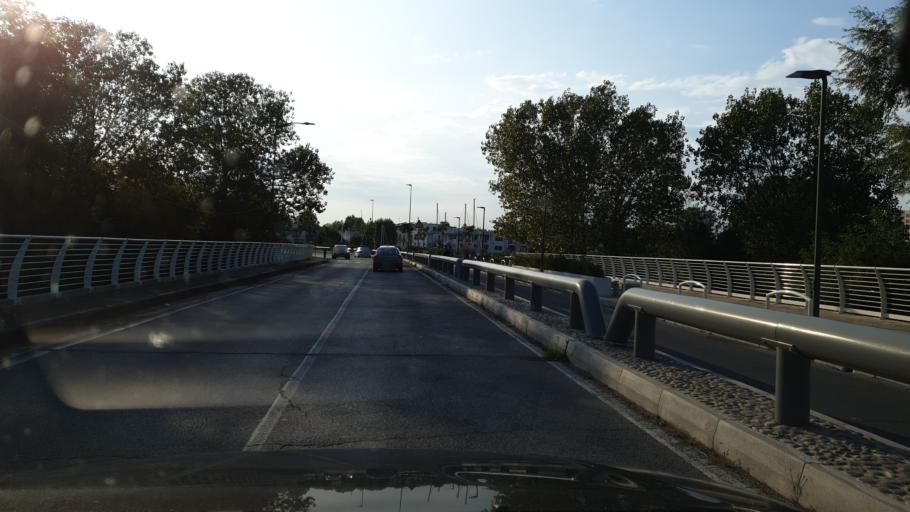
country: IT
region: Emilia-Romagna
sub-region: Provincia di Rimini
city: Montalbano
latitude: 43.9693
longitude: 12.7189
